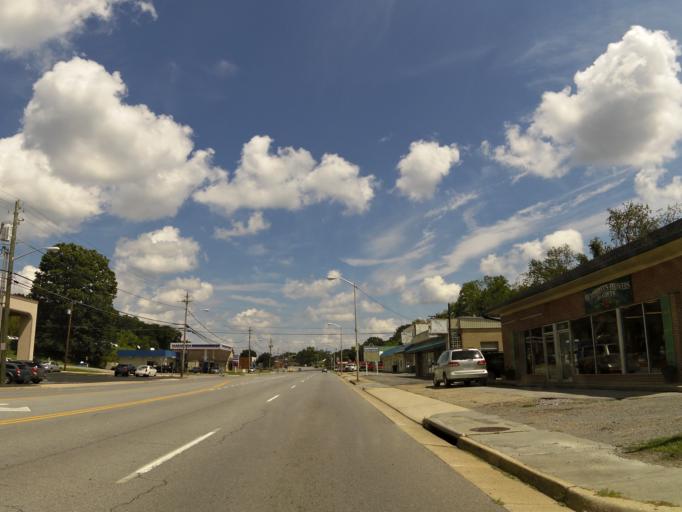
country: US
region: Virginia
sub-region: Washington County
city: Abingdon
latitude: 36.7062
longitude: -81.9918
